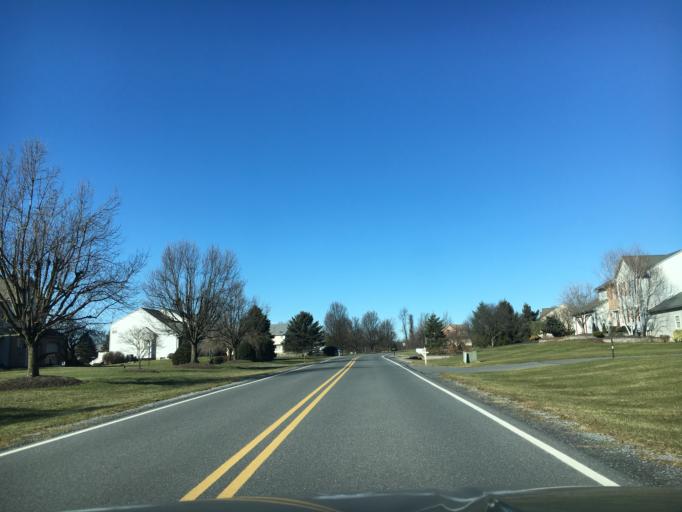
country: US
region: Pennsylvania
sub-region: Berks County
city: Fleetwood
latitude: 40.4260
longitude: -75.8298
